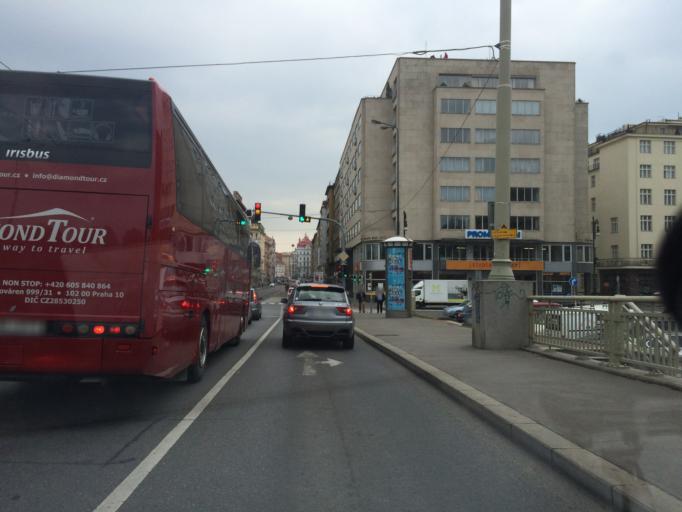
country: CZ
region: Praha
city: Prague
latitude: 50.0931
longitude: 14.4271
